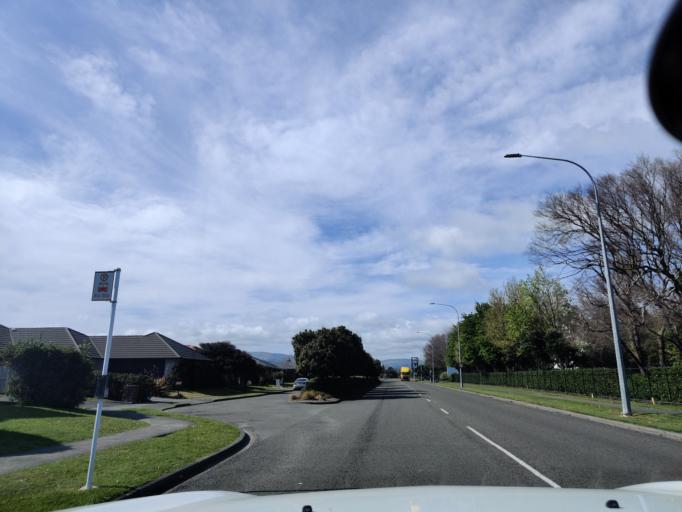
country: NZ
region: Manawatu-Wanganui
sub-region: Palmerston North City
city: Palmerston North
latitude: -40.3319
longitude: 175.6533
